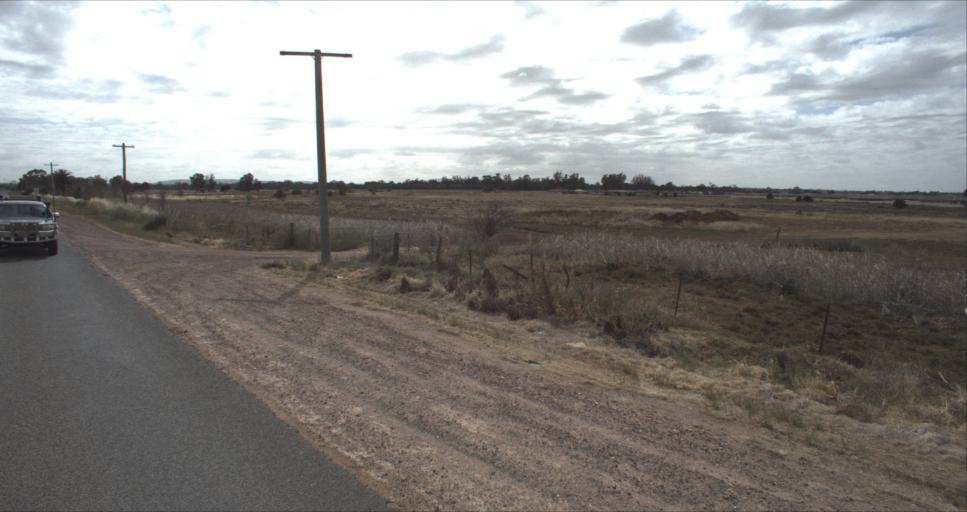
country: AU
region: New South Wales
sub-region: Leeton
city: Leeton
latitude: -34.5681
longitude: 146.3953
